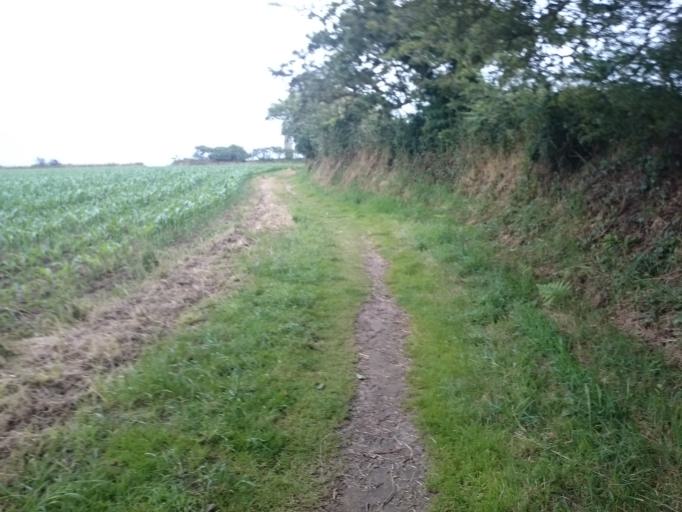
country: FR
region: Brittany
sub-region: Departement du Finistere
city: Ploumoguer
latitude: 48.4269
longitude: -4.6812
